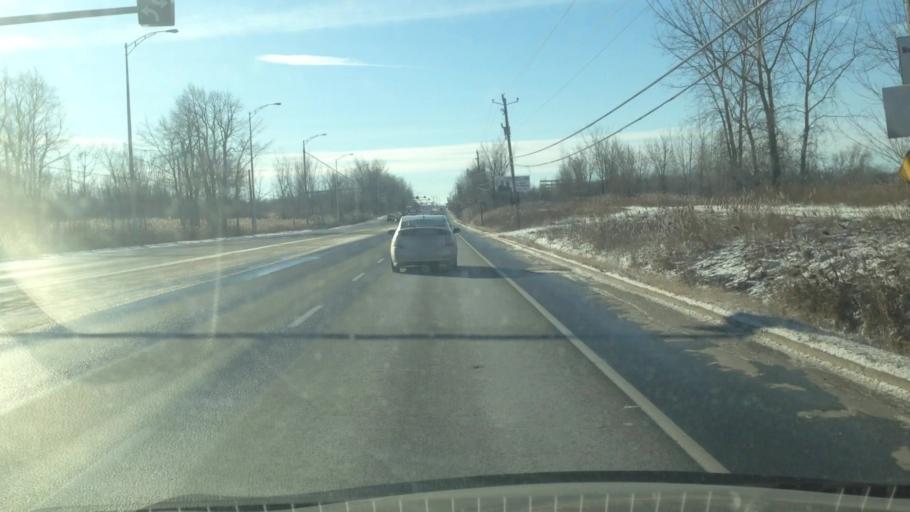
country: CA
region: Quebec
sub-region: Monteregie
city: Chateauguay
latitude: 45.3860
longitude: -73.7000
